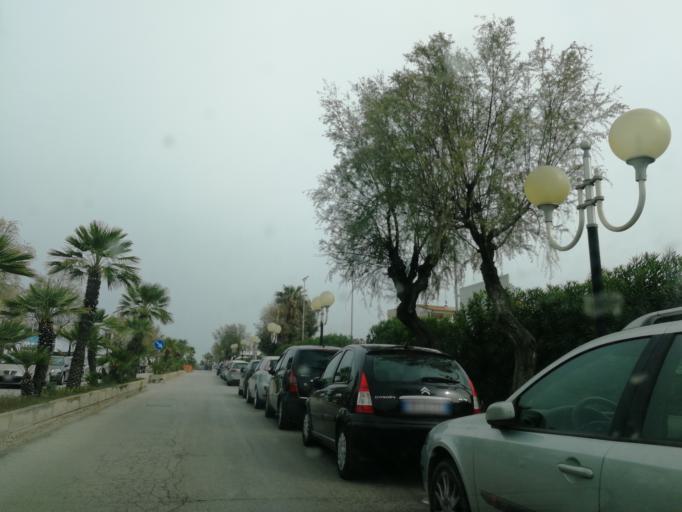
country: IT
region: Apulia
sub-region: Provincia di Barletta - Andria - Trani
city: Barletta
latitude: 41.3204
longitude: 16.2972
